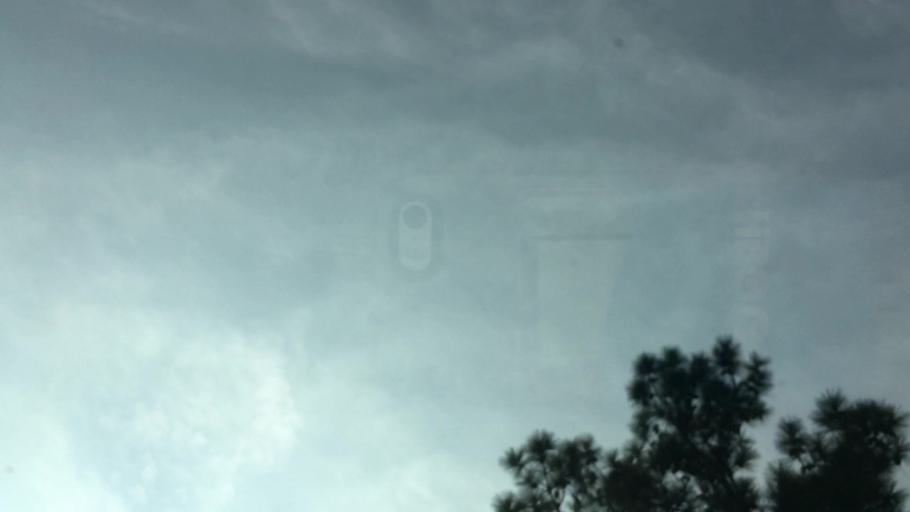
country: US
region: Alabama
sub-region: Bibb County
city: Woodstock
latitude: 33.2272
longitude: -87.1310
